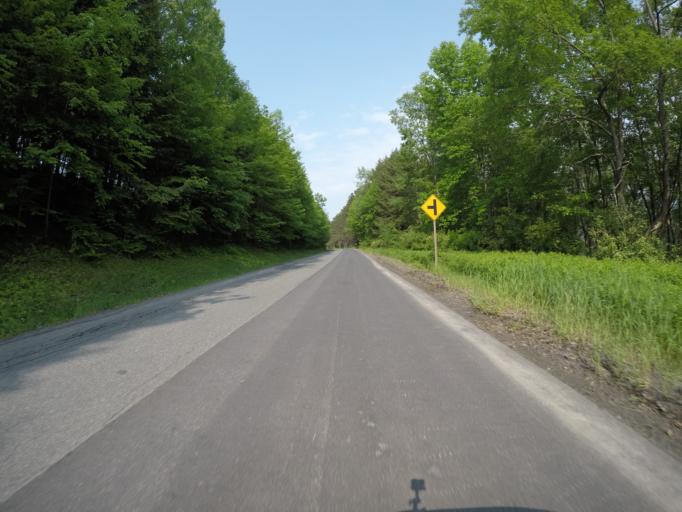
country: US
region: New York
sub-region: Sullivan County
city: Livingston Manor
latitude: 42.1101
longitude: -74.7367
